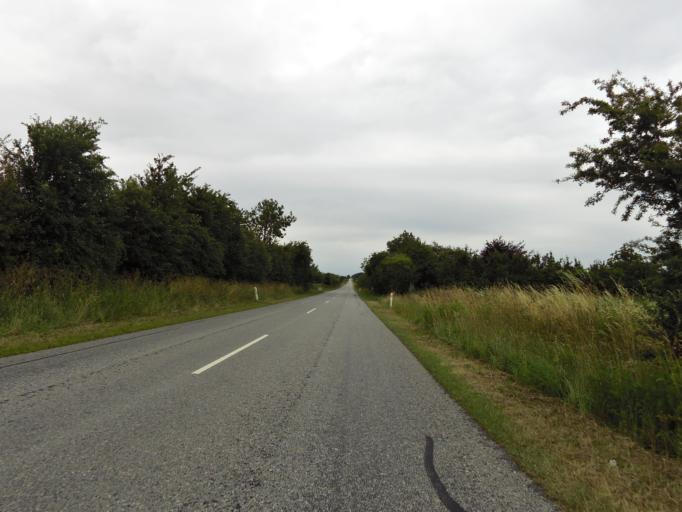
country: DK
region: South Denmark
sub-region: Tonder Kommune
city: Logumkloster
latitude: 55.1256
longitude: 8.9660
